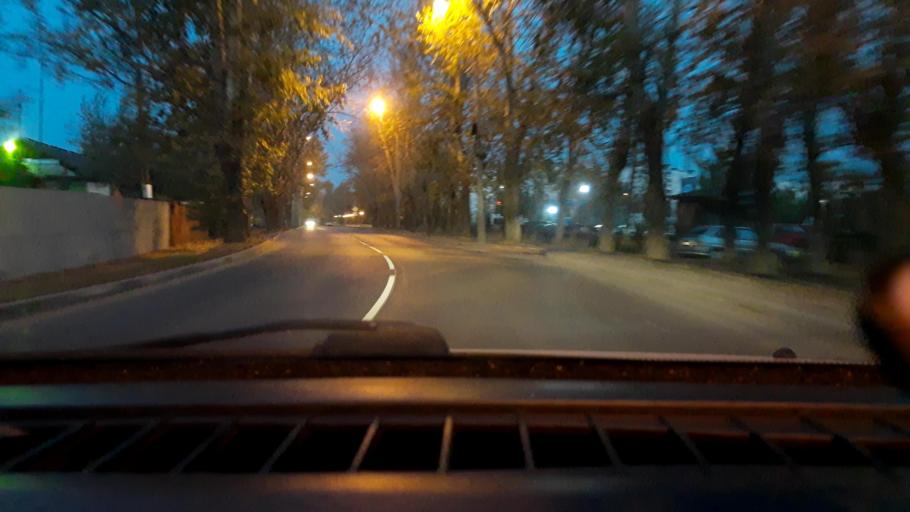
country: RU
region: Nizjnij Novgorod
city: Gorbatovka
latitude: 56.3427
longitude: 43.8108
